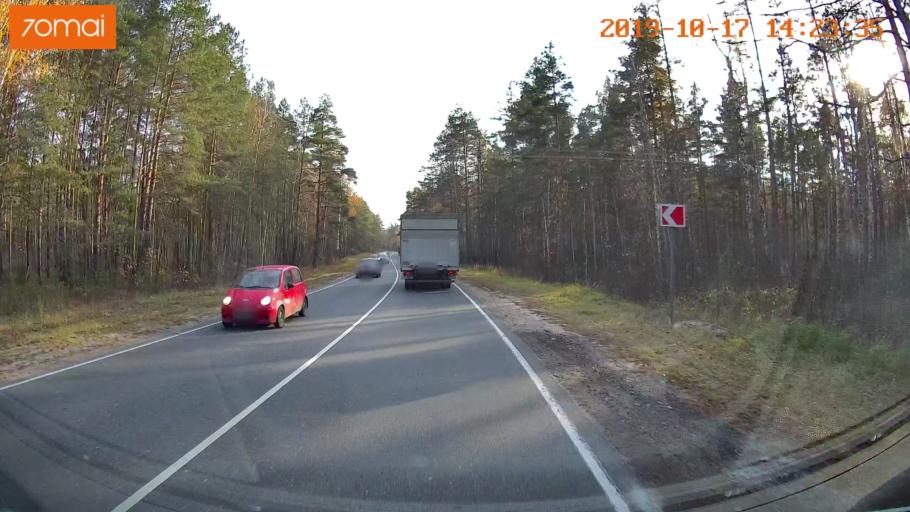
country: RU
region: Moskovskaya
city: Radovitskiy
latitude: 55.0174
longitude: 39.9613
